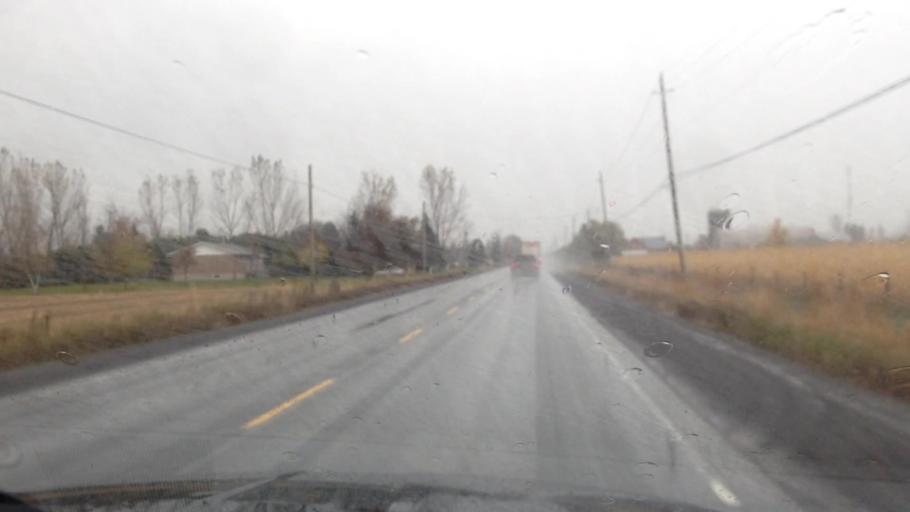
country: CA
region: Ontario
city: Bourget
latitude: 45.2861
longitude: -75.3201
